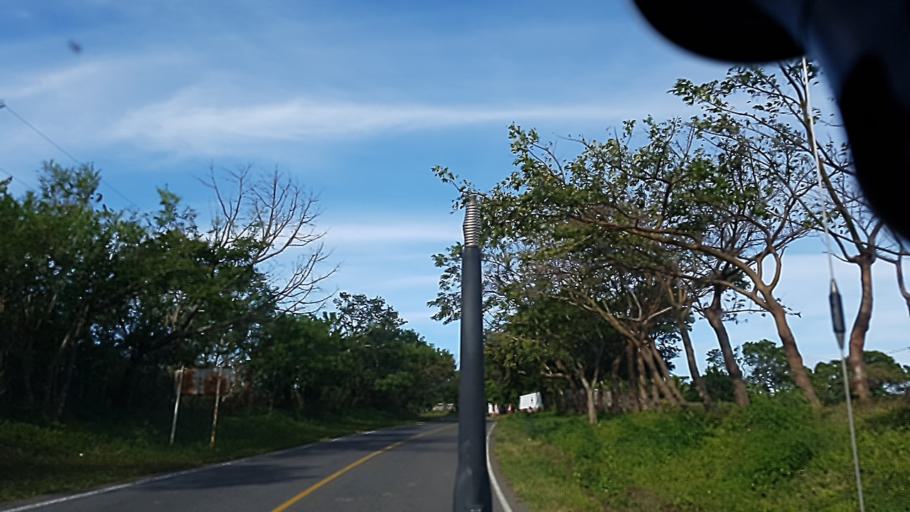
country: NI
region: Carazo
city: Santa Teresa
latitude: 11.7711
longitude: -86.1663
